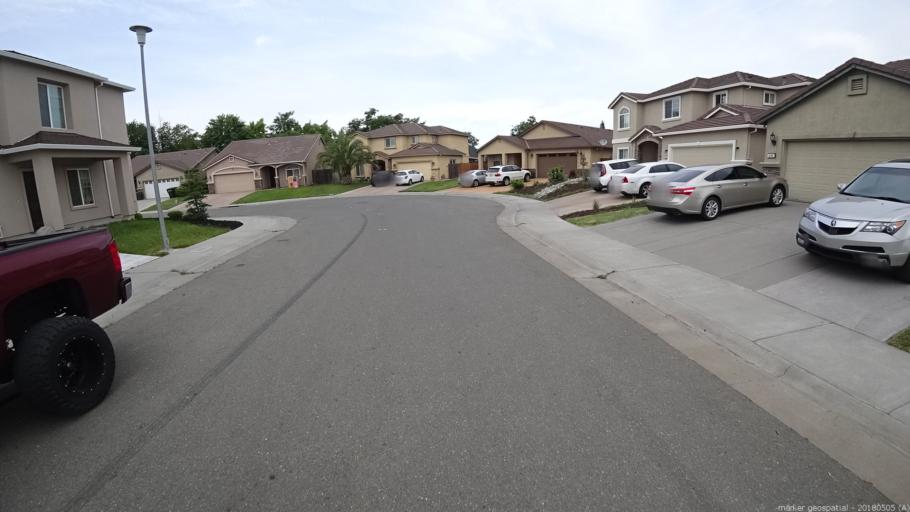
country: US
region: California
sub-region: Sacramento County
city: Rio Linda
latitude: 38.6453
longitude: -121.4400
